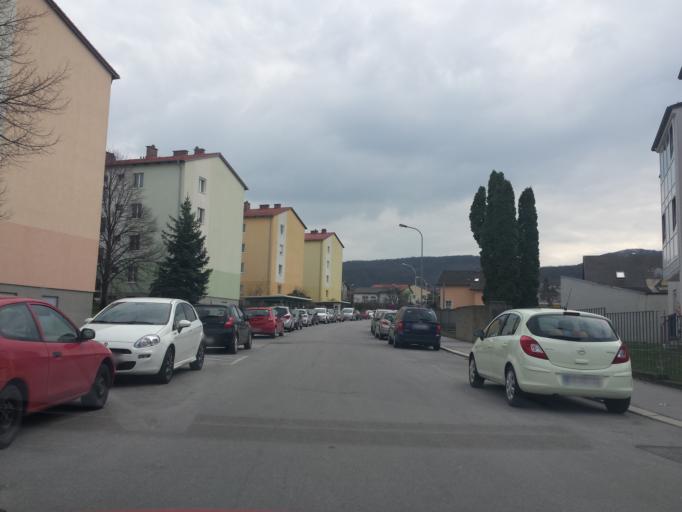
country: AT
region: Lower Austria
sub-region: Politischer Bezirk Bruck an der Leitha
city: Hainburg an der Donau
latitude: 48.1444
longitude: 16.9549
